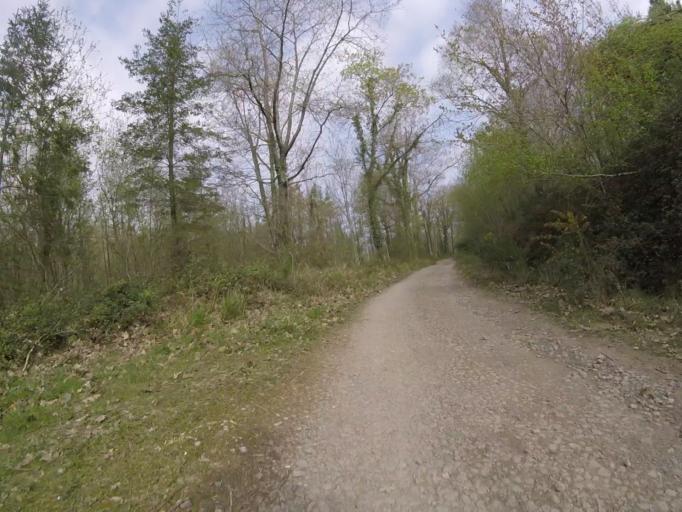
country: ES
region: Basque Country
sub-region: Provincia de Guipuzcoa
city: Usurbil
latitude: 43.2459
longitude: -2.0841
